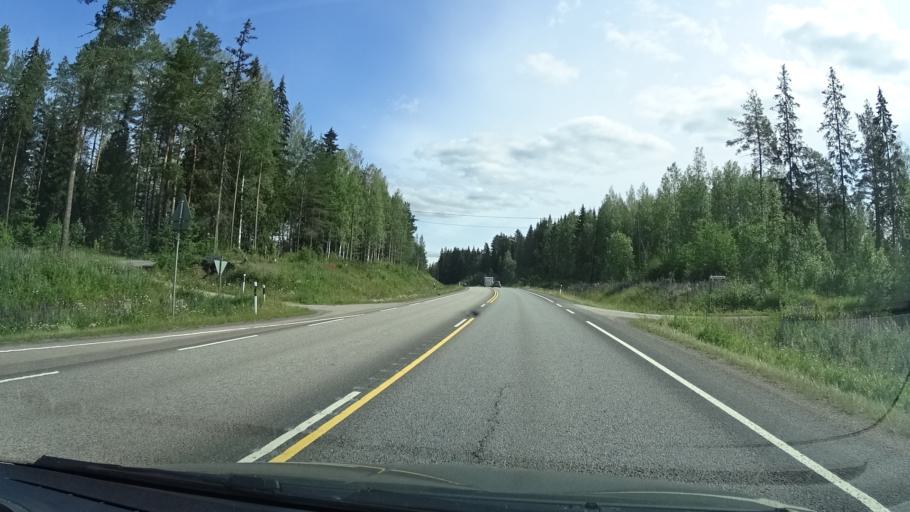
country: FI
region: Central Finland
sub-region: Jyvaeskylae
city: Muurame
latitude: 62.2668
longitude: 25.4989
